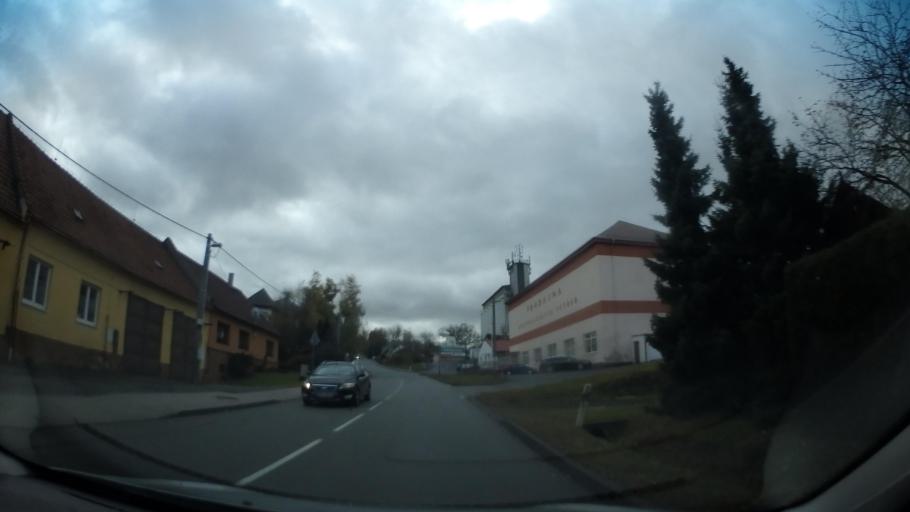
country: CZ
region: Vysocina
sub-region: Okres Zd'ar nad Sazavou
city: Velka Bites
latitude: 49.2843
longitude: 16.2266
